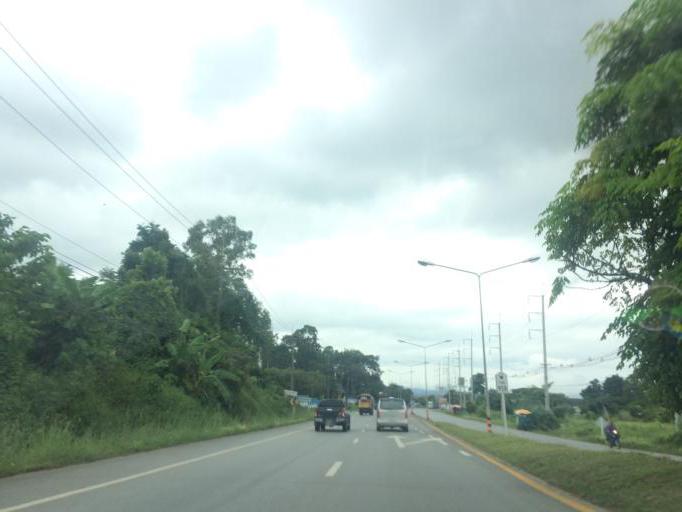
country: TH
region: Chiang Rai
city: Mae Chan
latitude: 20.1277
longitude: 99.8663
